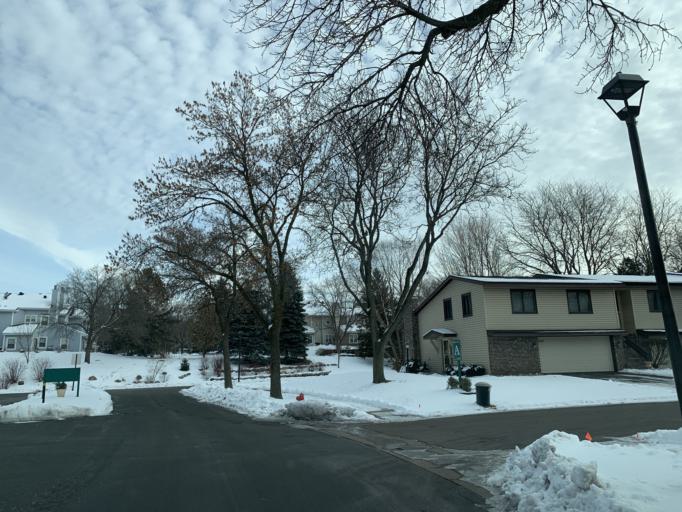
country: US
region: Minnesota
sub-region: Scott County
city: Savage
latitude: 44.8279
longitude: -93.3536
